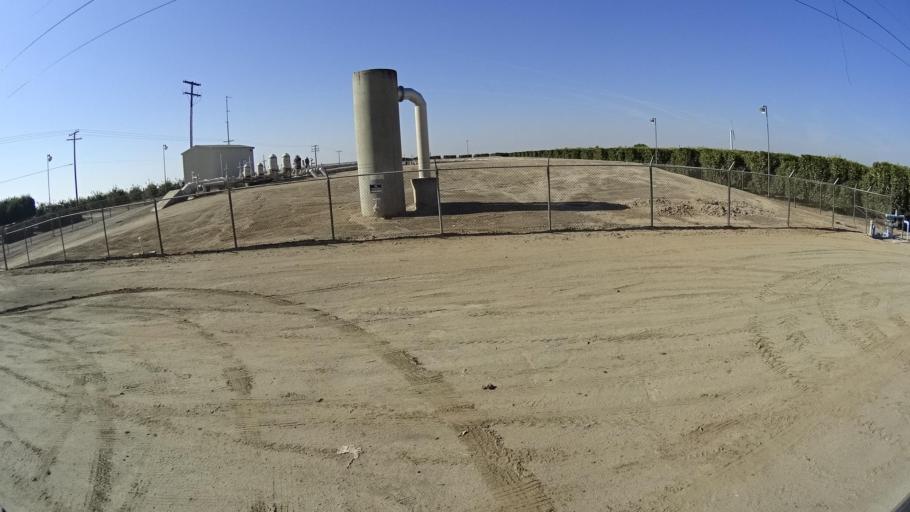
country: US
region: California
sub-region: Tulare County
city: Richgrove
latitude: 35.7184
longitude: -119.1428
